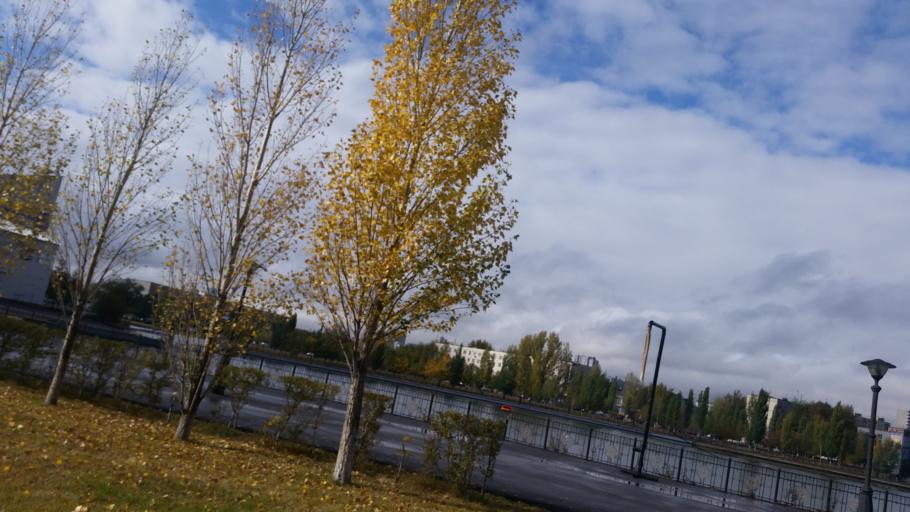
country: KZ
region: Astana Qalasy
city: Astana
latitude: 51.1542
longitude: 71.4573
